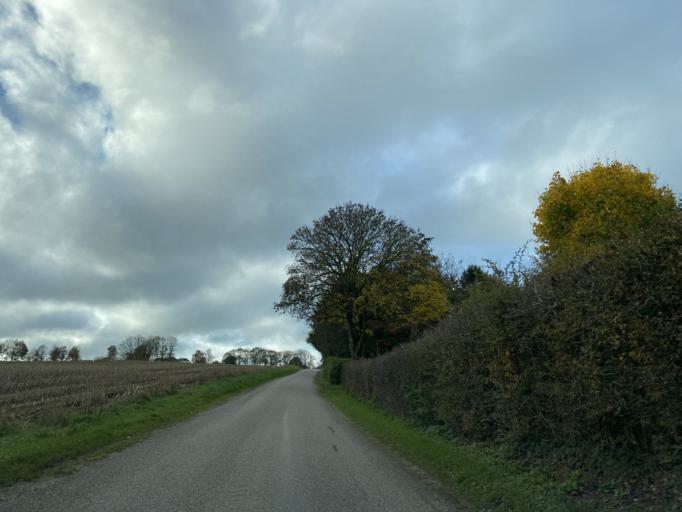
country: DK
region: Central Jutland
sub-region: Favrskov Kommune
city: Hammel
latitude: 56.2544
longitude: 9.7843
